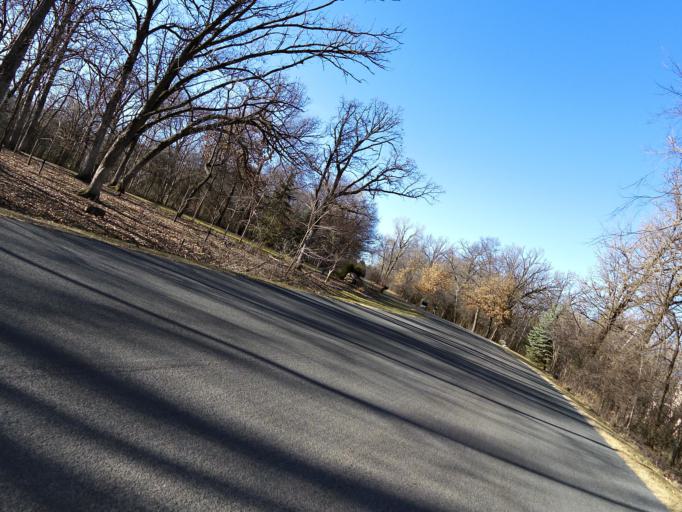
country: US
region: Minnesota
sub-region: Washington County
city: Bayport
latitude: 44.9826
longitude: -92.8022
